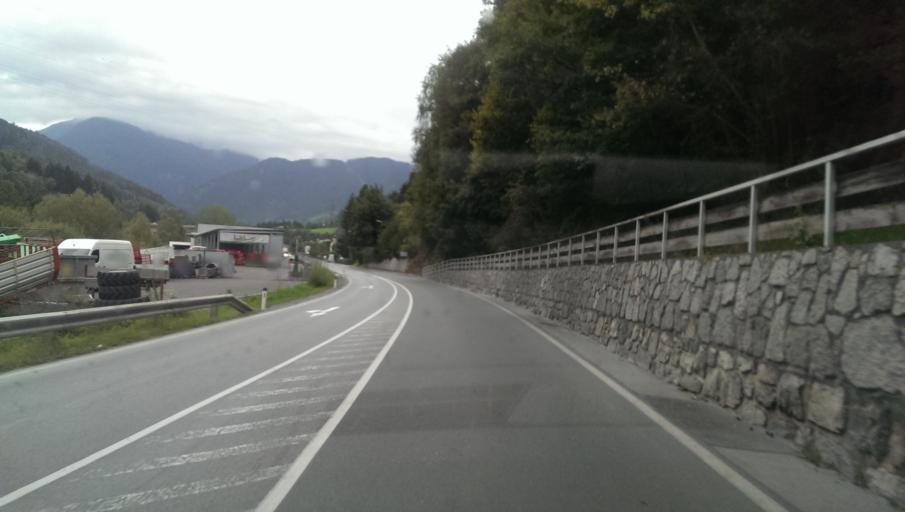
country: AT
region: Tyrol
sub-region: Politischer Bezirk Landeck
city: Stanz bei Landeck
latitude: 47.1412
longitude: 10.5416
